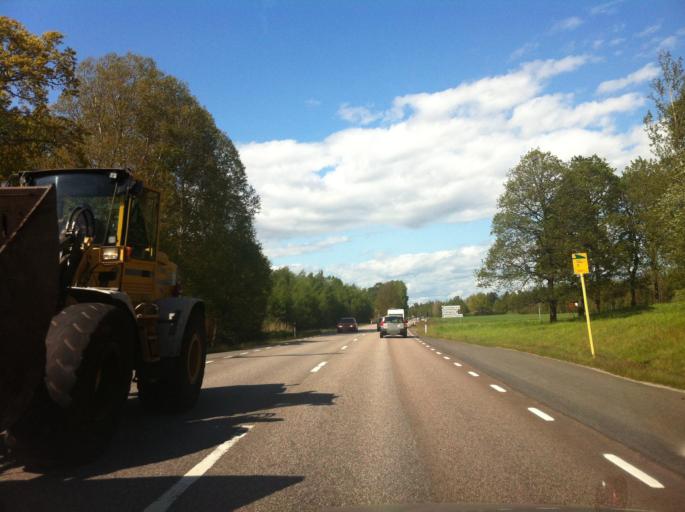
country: SE
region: Vaermland
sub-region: Kristinehamns Kommun
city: Bjorneborg
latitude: 59.1266
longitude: 14.1760
